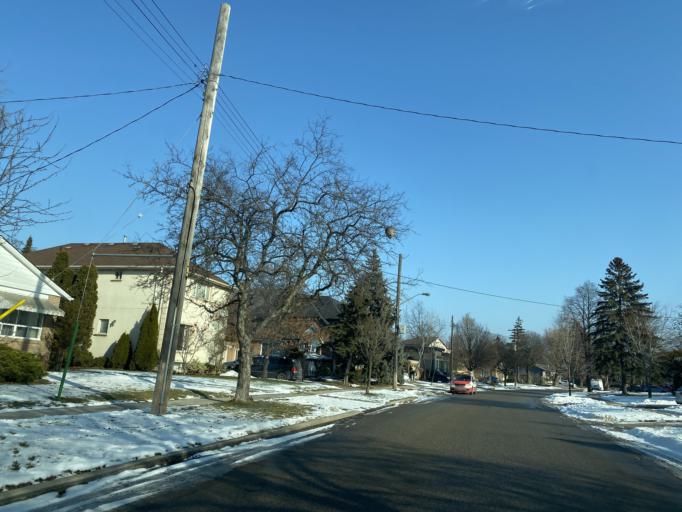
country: CA
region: Ontario
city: Etobicoke
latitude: 43.6658
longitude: -79.5627
